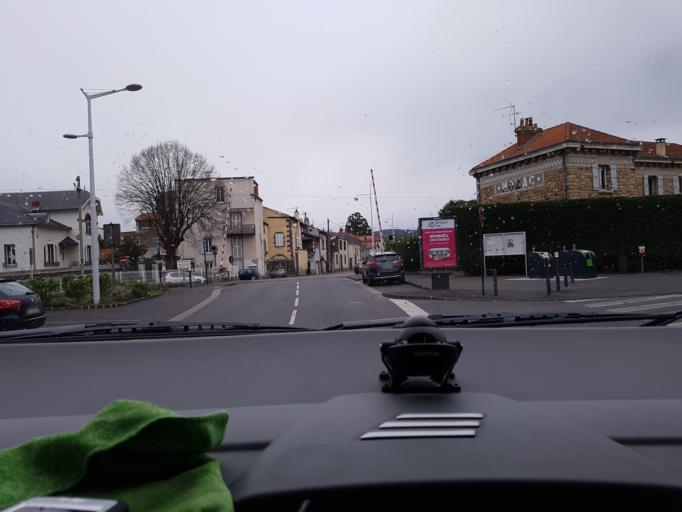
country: FR
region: Auvergne
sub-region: Departement du Puy-de-Dome
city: Mozac
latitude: 45.8933
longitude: 3.1046
